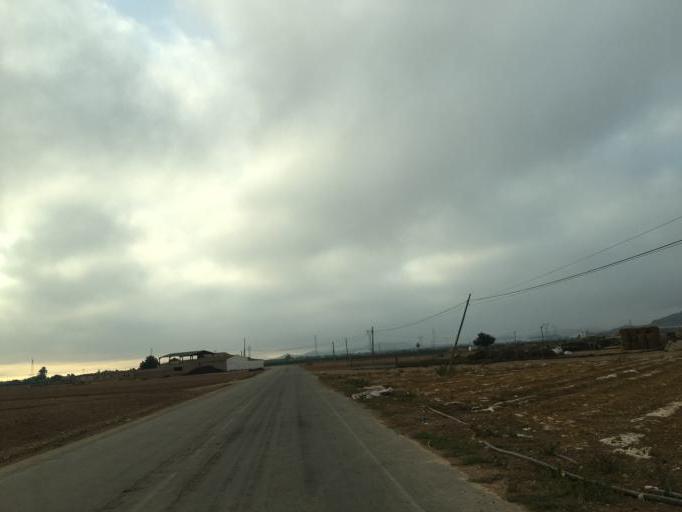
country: ES
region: Murcia
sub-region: Murcia
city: Cartagena
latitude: 37.6631
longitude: -0.9468
